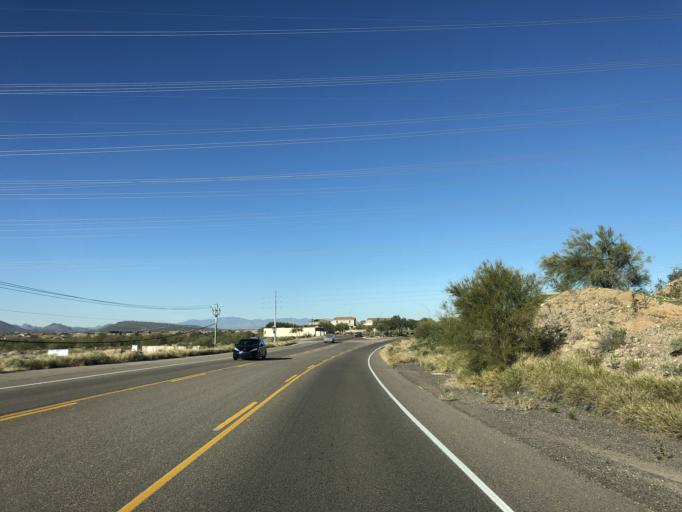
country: US
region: Arizona
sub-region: Maricopa County
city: Sun City West
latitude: 33.7056
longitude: -112.2897
